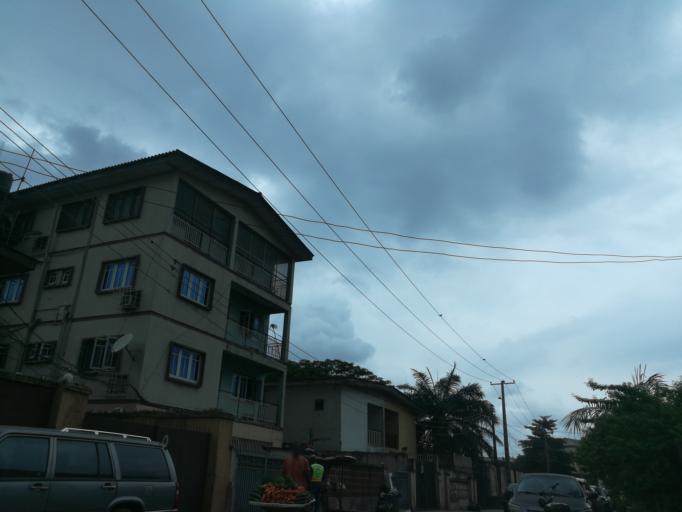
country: NG
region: Lagos
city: Ikeja
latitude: 6.6008
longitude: 3.3473
